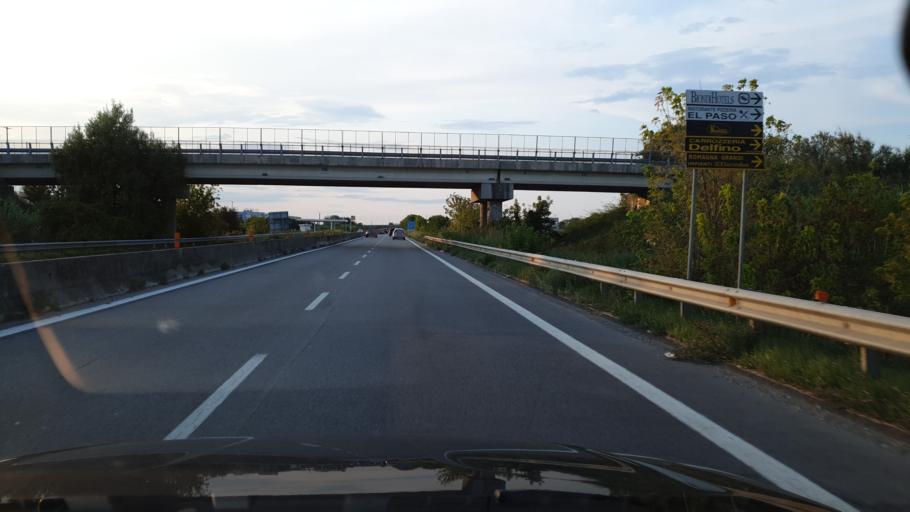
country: IT
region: Emilia-Romagna
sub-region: Forli-Cesena
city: Gatteo a Mare
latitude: 44.1728
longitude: 12.4192
